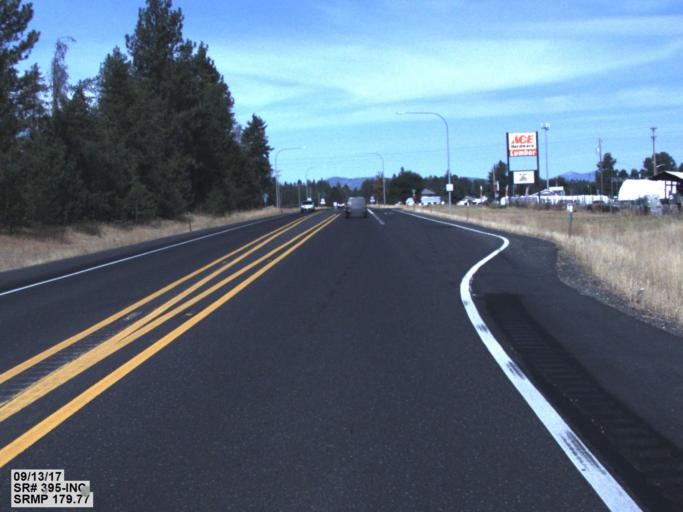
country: US
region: Washington
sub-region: Spokane County
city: Deer Park
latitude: 47.9456
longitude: -117.4802
